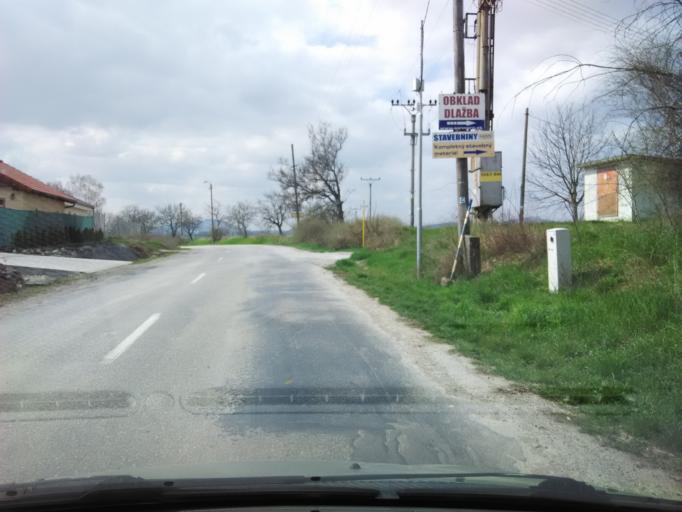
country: SK
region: Nitriansky
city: Zlate Moravce
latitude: 48.3860
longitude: 18.3186
